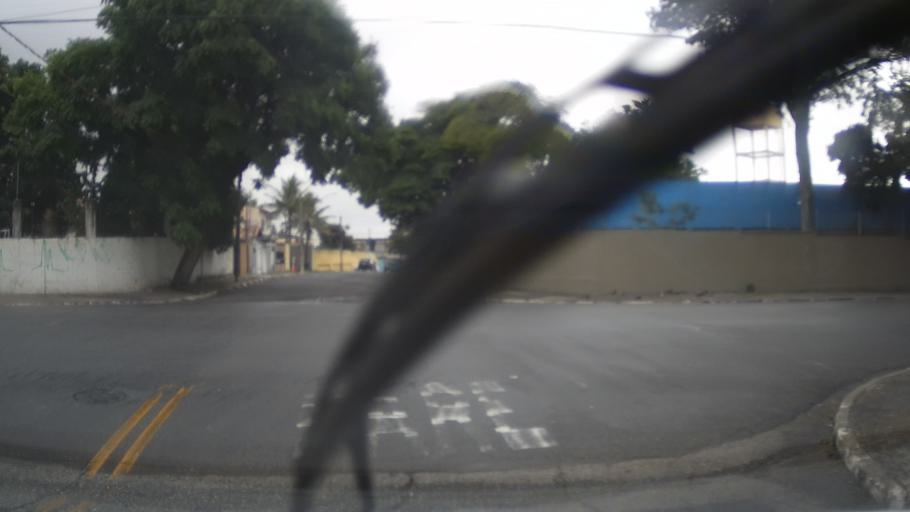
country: BR
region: Sao Paulo
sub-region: Guarulhos
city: Guarulhos
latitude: -23.4674
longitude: -46.5594
